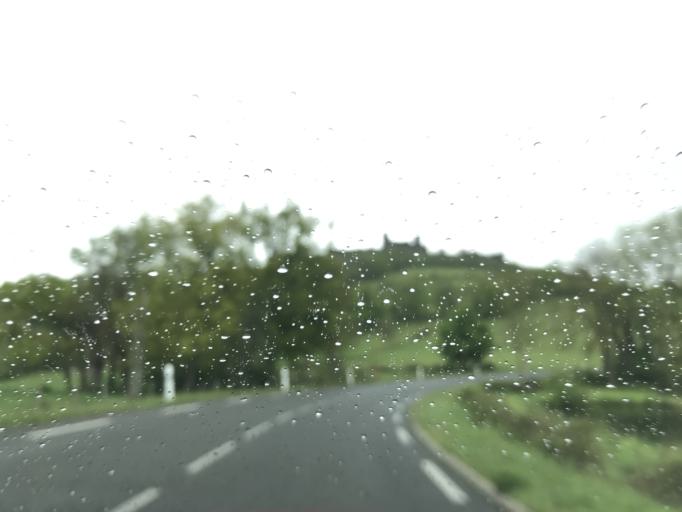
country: FR
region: Auvergne
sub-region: Departement du Puy-de-Dome
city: Billom
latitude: 45.7058
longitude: 3.4204
